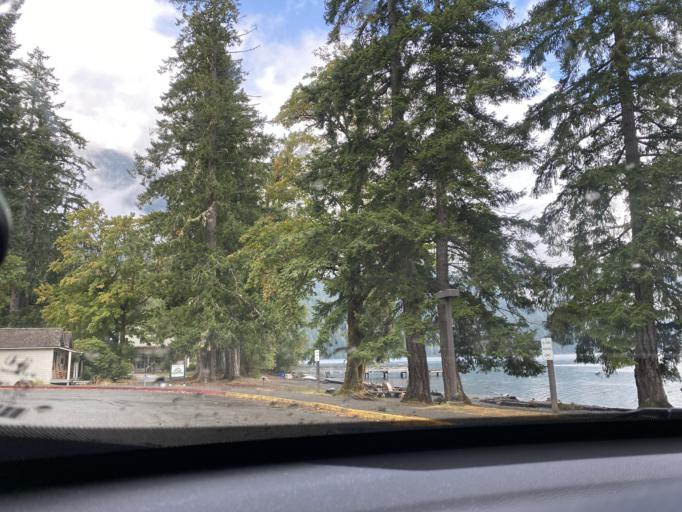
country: CA
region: British Columbia
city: Sooke
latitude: 48.0582
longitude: -123.7992
